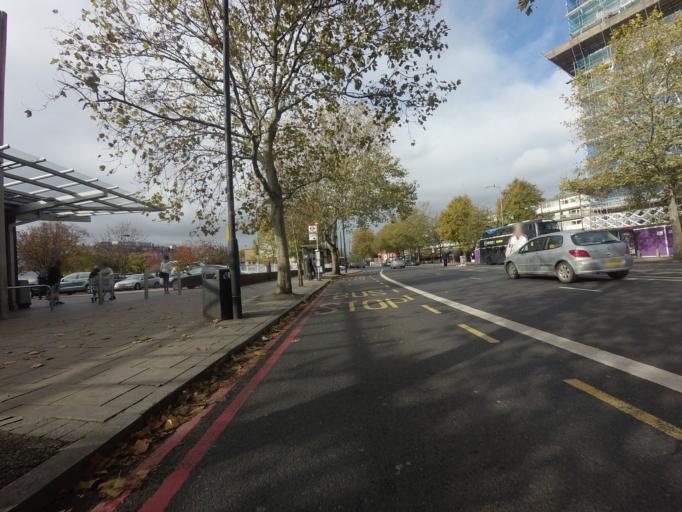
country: GB
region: England
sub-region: Greater London
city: Camberwell
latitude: 51.4790
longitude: -0.0558
